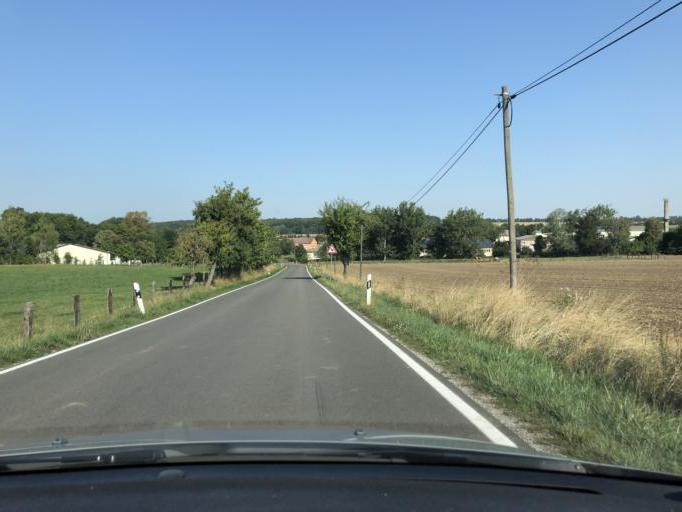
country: DE
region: Thuringia
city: Rastenberg
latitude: 51.1990
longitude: 11.4623
